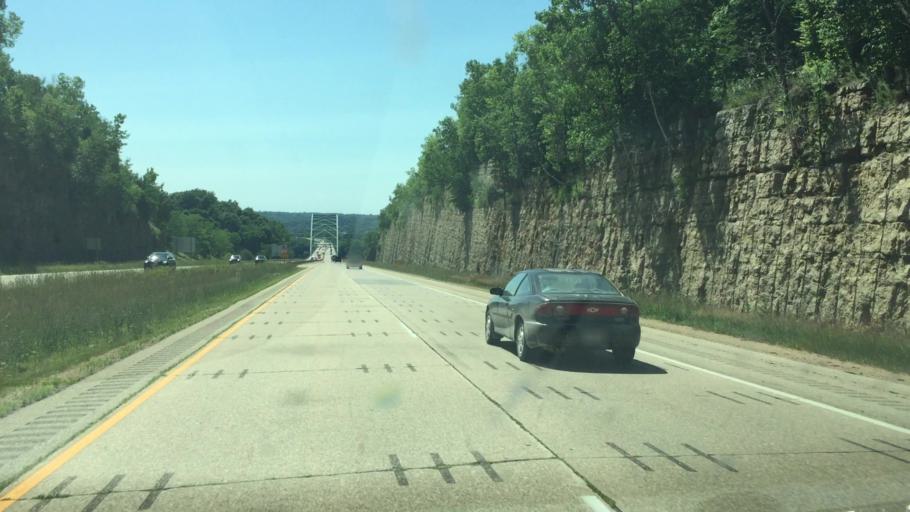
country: US
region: Illinois
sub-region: Jo Daviess County
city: East Dubuque
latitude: 42.5154
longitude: -90.6242
